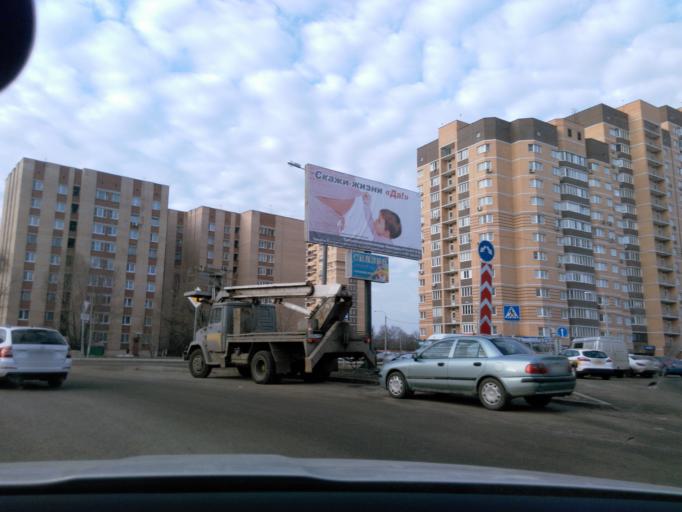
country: RU
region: Moskovskaya
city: Dolgoprudnyy
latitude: 55.9382
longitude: 37.4915
